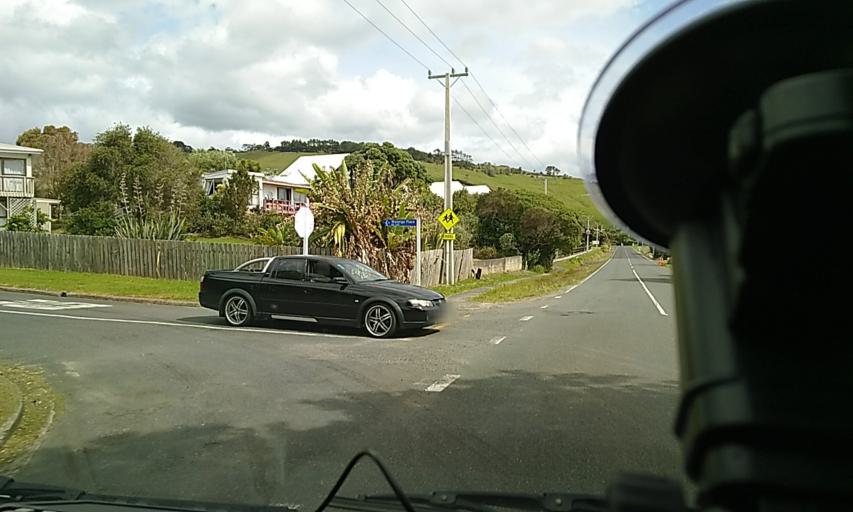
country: NZ
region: Northland
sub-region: Far North District
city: Ahipara
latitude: -35.5273
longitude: 173.3898
